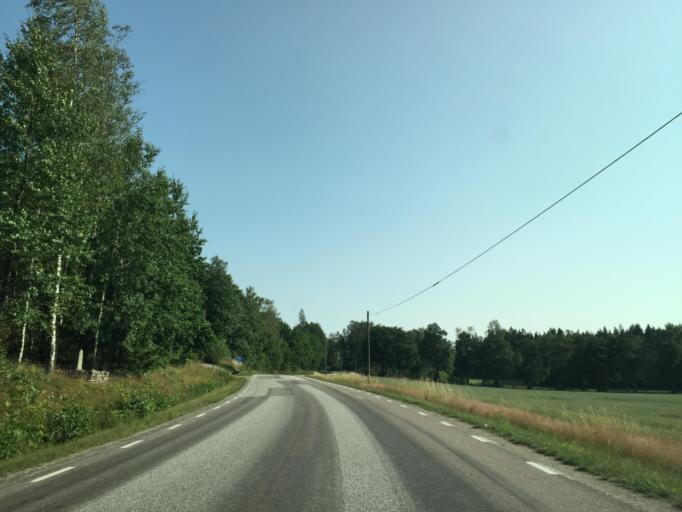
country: SE
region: Vaestra Goetaland
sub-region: Trollhattan
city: Trollhattan
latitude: 58.3214
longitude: 12.2573
